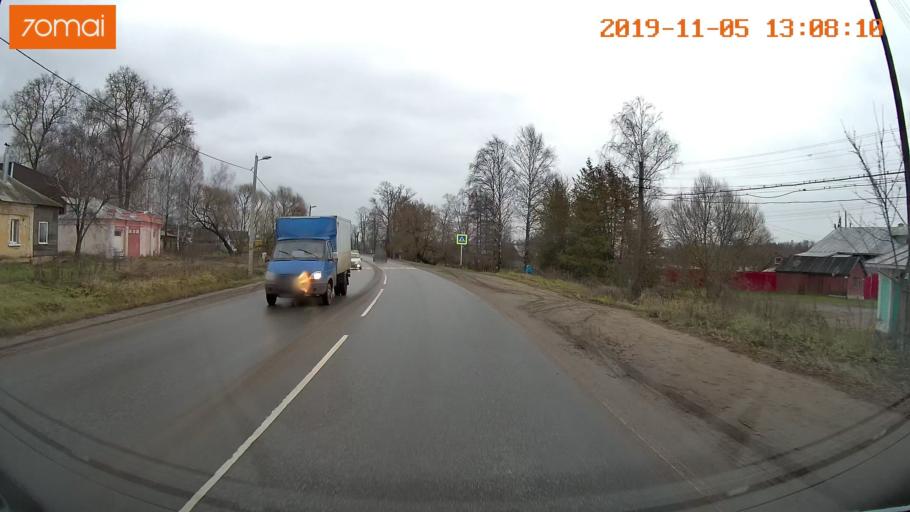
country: RU
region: Ivanovo
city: Kitovo
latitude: 56.8647
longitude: 41.2885
